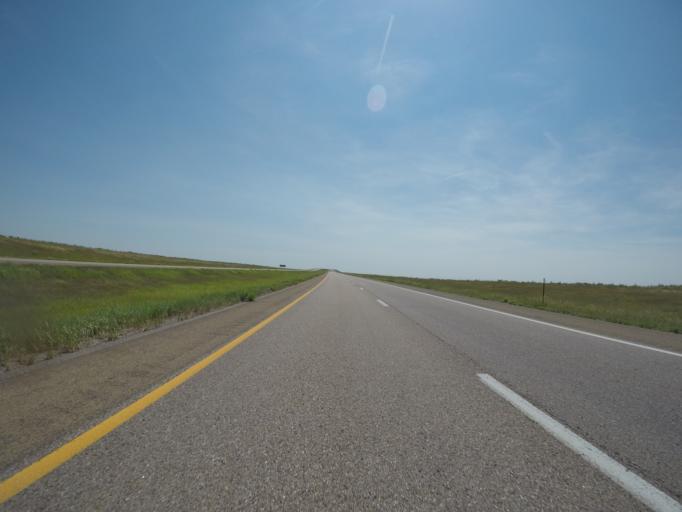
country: US
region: Kansas
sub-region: Thomas County
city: Colby
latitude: 39.3165
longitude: -100.9862
